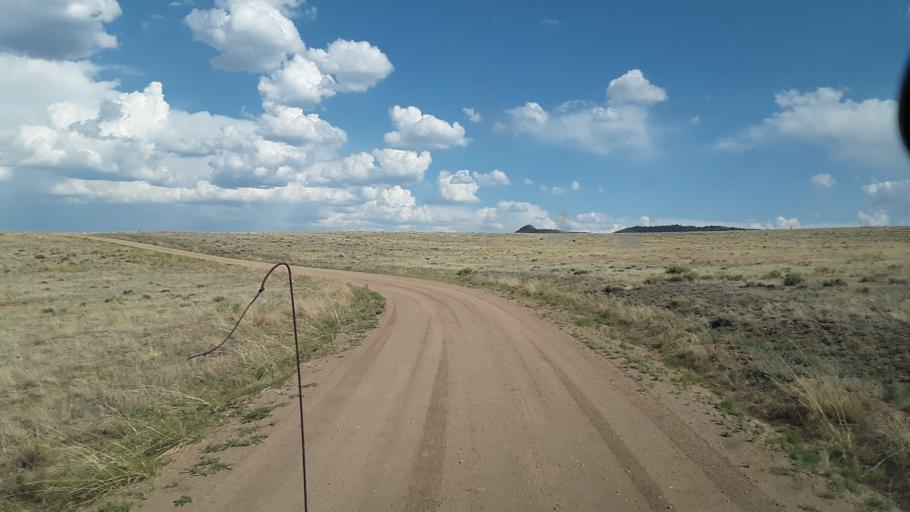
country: US
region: Colorado
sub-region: Custer County
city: Westcliffe
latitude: 38.2717
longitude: -105.4716
